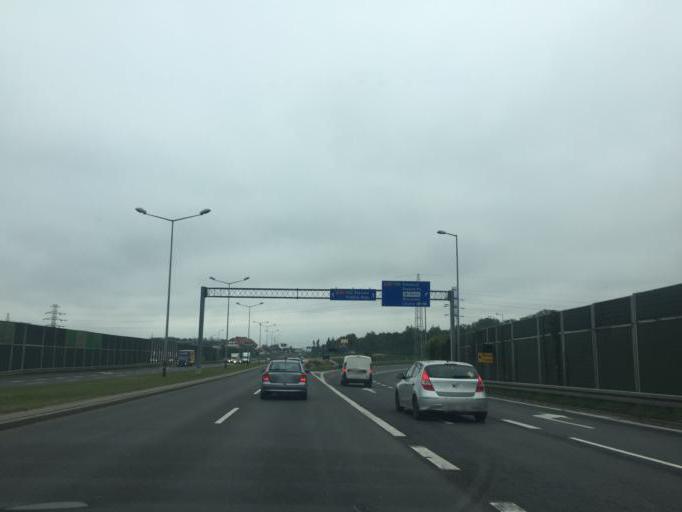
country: PL
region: Lesser Poland Voivodeship
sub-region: Powiat wielicki
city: Czarnochowice
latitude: 50.0068
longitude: 20.0162
